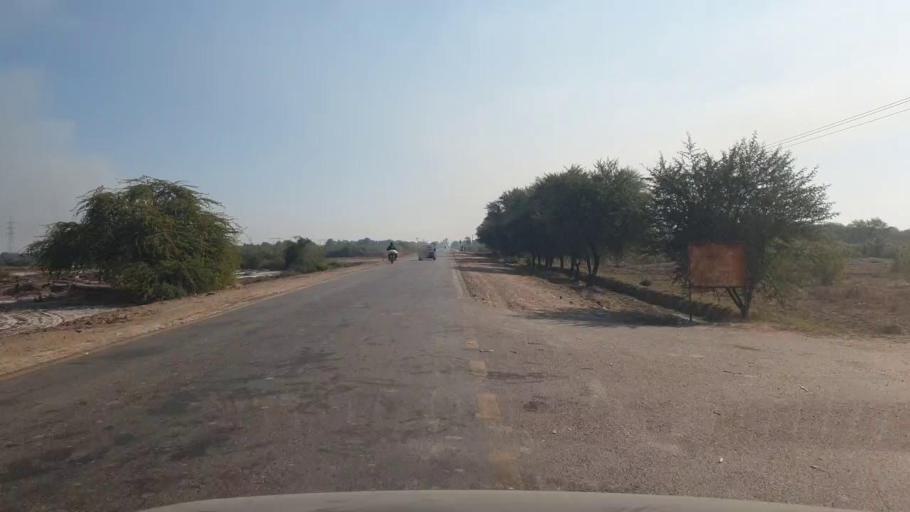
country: PK
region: Sindh
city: Mirwah Gorchani
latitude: 25.3026
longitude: 69.0889
